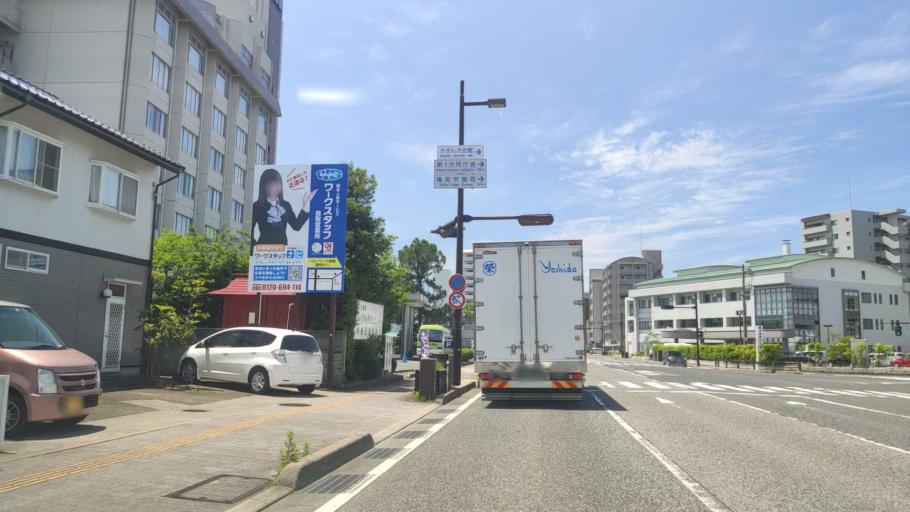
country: JP
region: Tottori
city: Tottori
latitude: 35.4896
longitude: 134.2279
